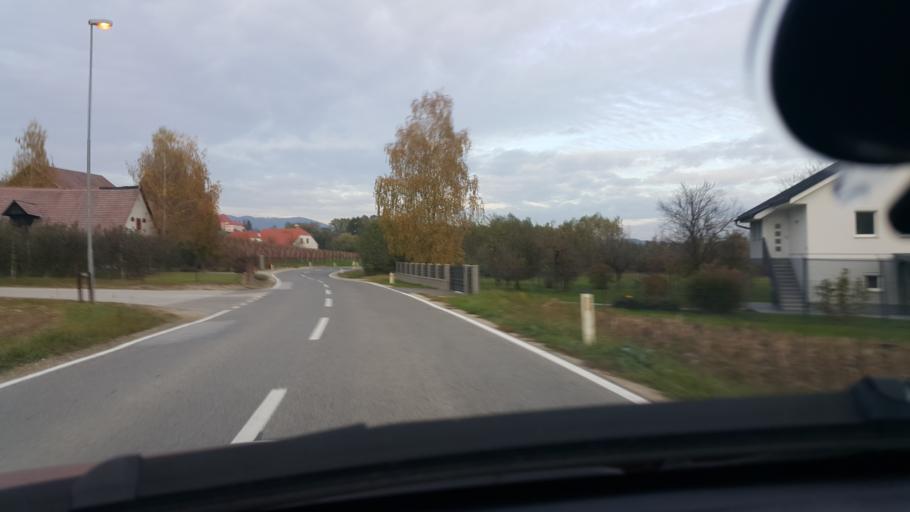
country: SI
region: Bistrica ob Sotli
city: Bistrica ob Sotli
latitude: 46.0088
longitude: 15.6922
